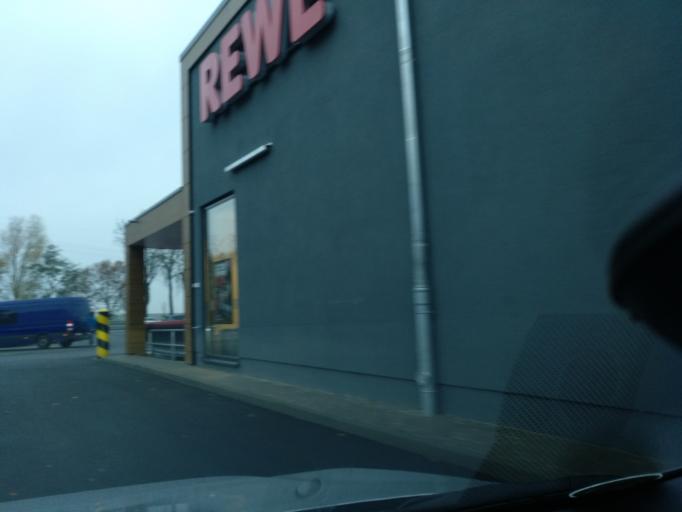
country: DE
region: Brandenburg
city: Hoppegarten
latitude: 52.5017
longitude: 13.6896
